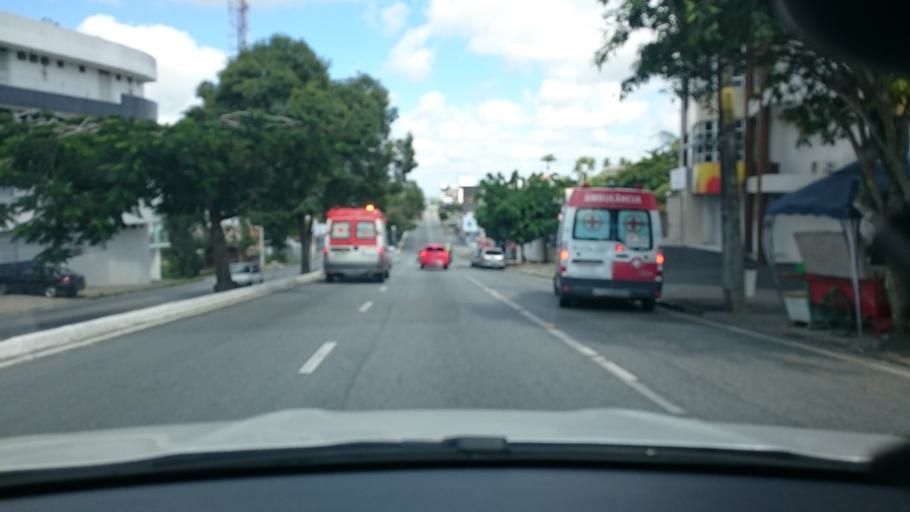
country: BR
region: Paraiba
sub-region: Campina Grande
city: Campina Grande
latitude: -7.2251
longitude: -35.8961
